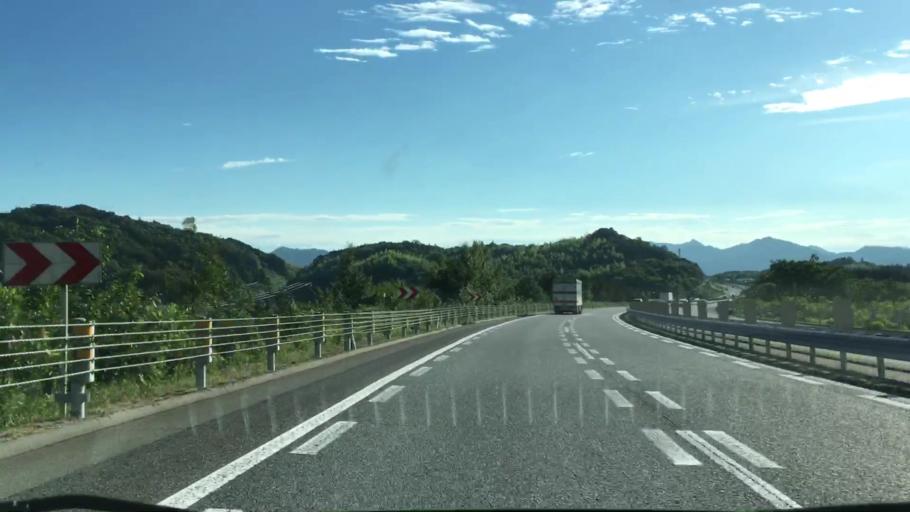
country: JP
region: Yamaguchi
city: Iwakuni
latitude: 34.1043
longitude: 132.1113
